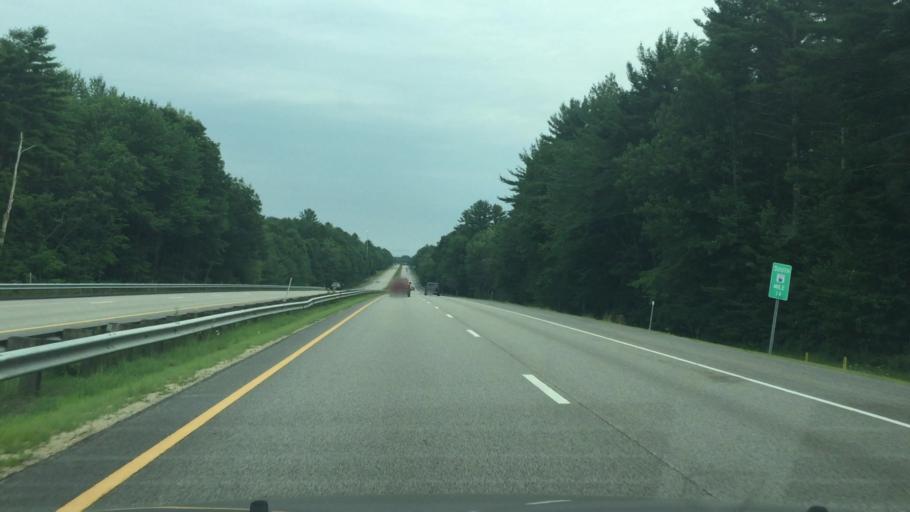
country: US
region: New Hampshire
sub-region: Strafford County
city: Somersworth
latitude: 43.2367
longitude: -70.9164
